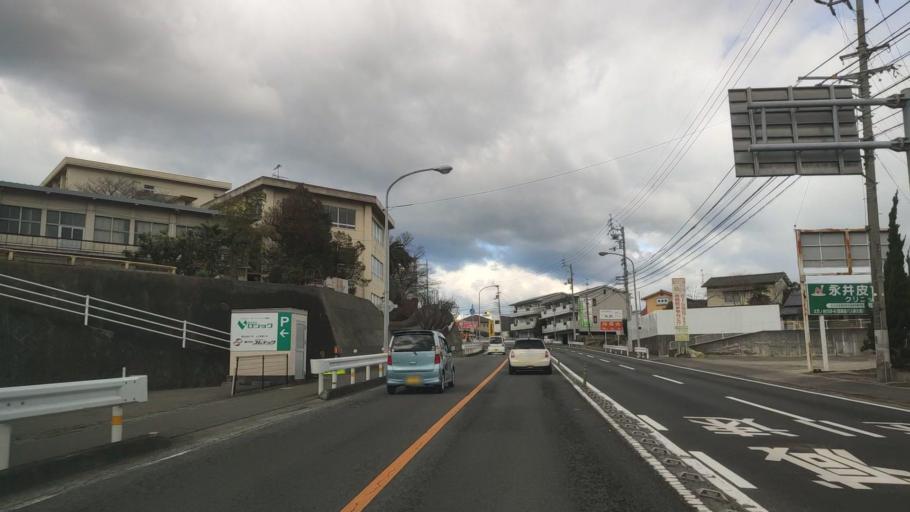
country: JP
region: Ehime
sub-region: Shikoku-chuo Shi
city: Matsuyama
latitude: 33.8562
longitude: 132.7425
